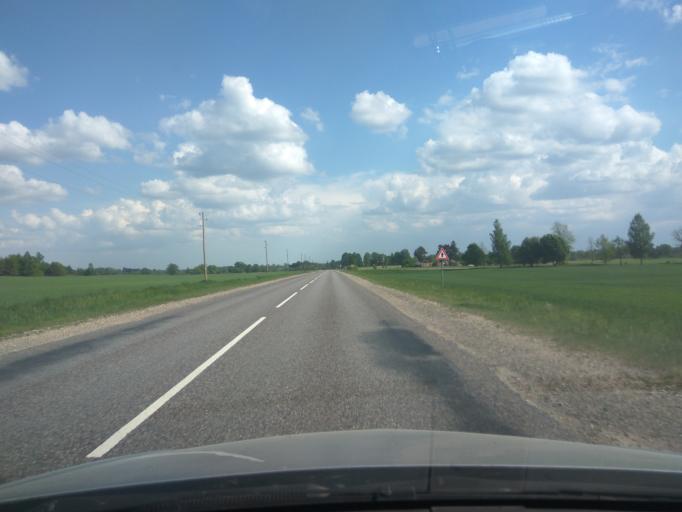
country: LV
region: Kuldigas Rajons
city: Kuldiga
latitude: 57.0246
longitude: 21.8616
